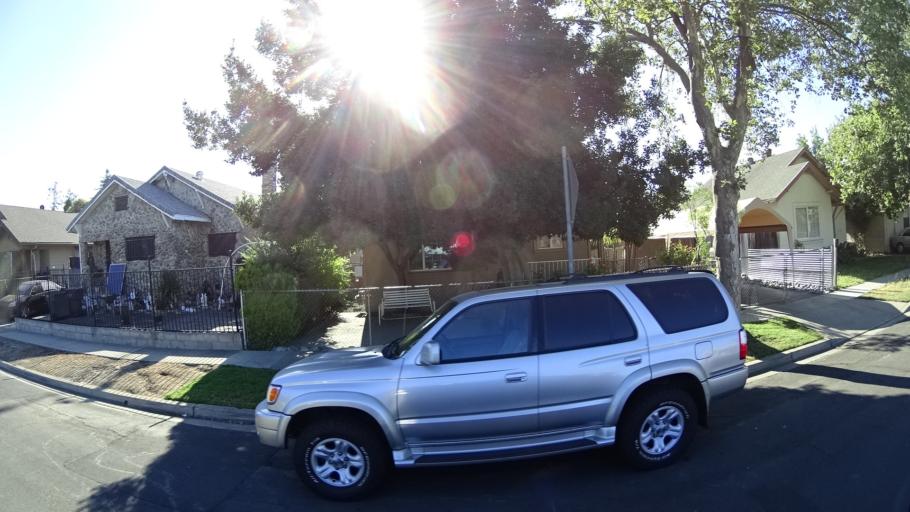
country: US
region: California
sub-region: Sacramento County
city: Parkway
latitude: 38.5336
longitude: -121.4456
